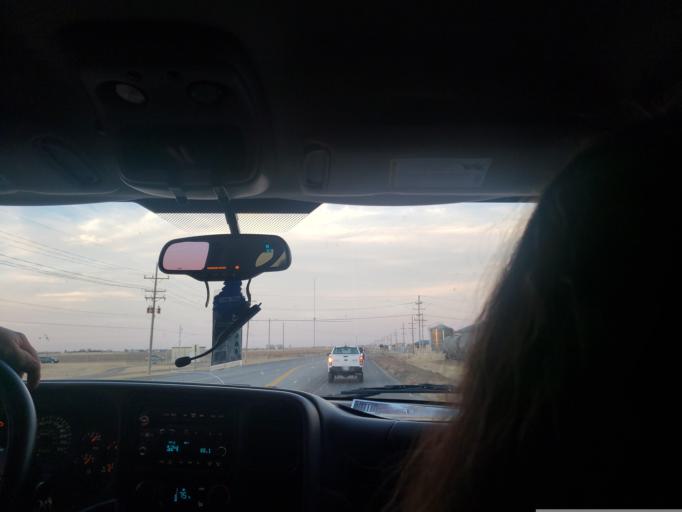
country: US
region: Kansas
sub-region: Seward County
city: Liberal
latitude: 37.0525
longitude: -100.9041
